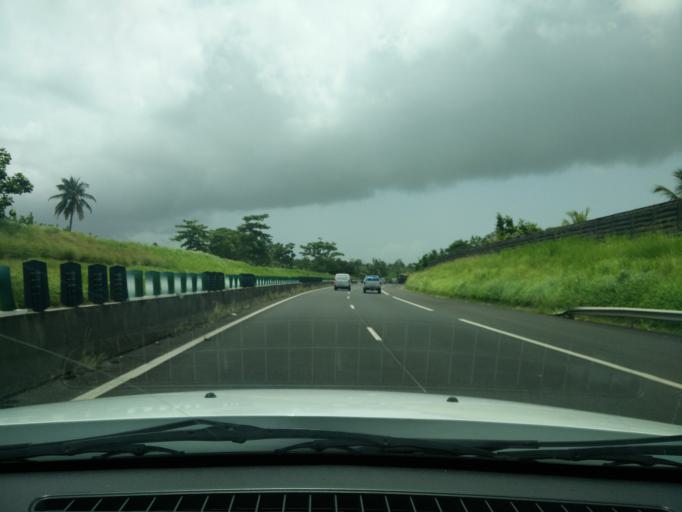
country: GP
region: Guadeloupe
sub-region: Guadeloupe
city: Capesterre-Belle-Eau
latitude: 16.0419
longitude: -61.5764
